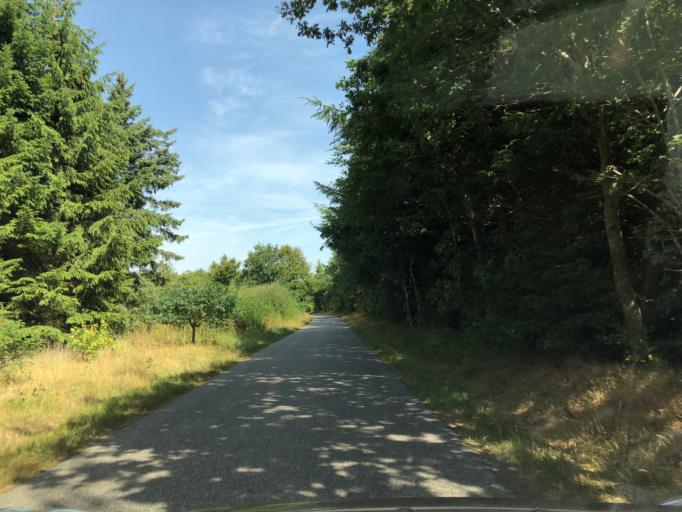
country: DK
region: Central Jutland
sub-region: Ringkobing-Skjern Kommune
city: Skjern
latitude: 55.9648
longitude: 8.4798
